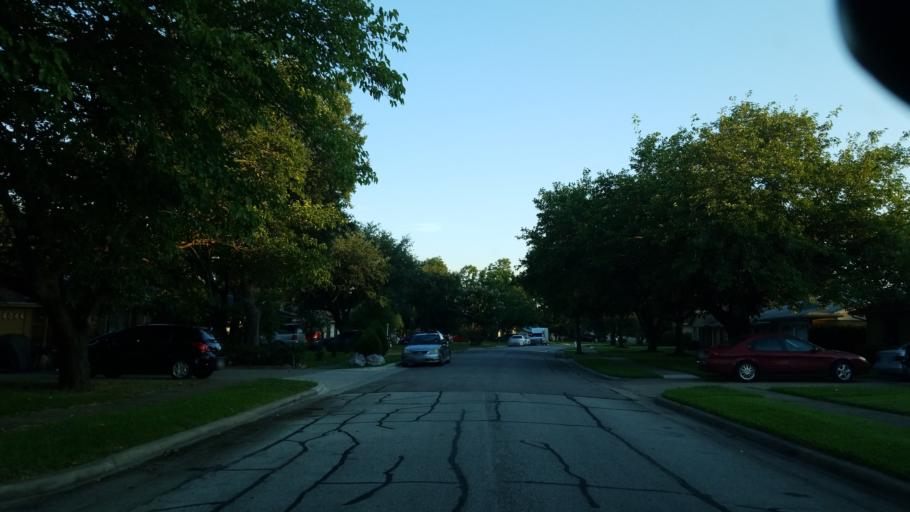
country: US
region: Texas
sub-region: Dallas County
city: Farmers Branch
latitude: 32.9369
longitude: -96.8830
